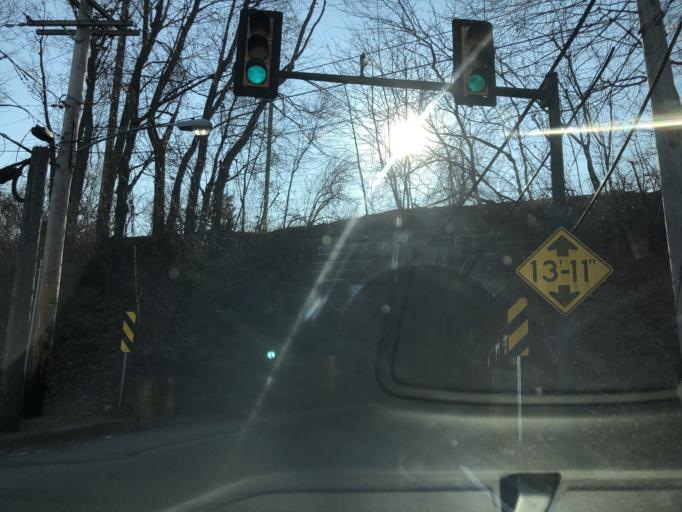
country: US
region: Pennsylvania
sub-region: Chester County
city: Downingtown
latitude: 40.0030
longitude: -75.7078
